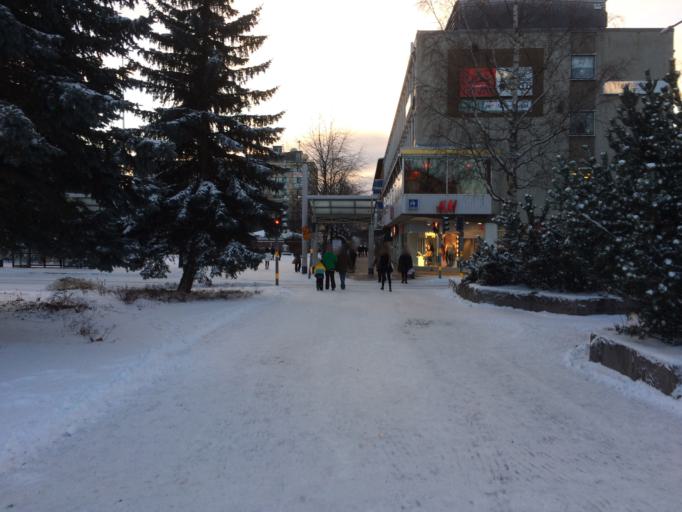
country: SE
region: Vaesterbotten
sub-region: Skelleftea Kommun
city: Skelleftea
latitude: 64.7519
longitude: 20.9532
